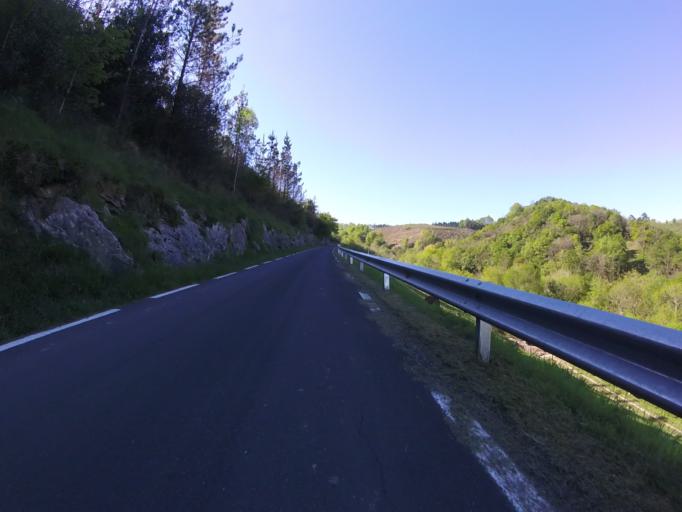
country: ES
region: Basque Country
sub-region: Provincia de Guipuzcoa
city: Aizarnazabal
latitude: 43.2232
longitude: -2.2130
